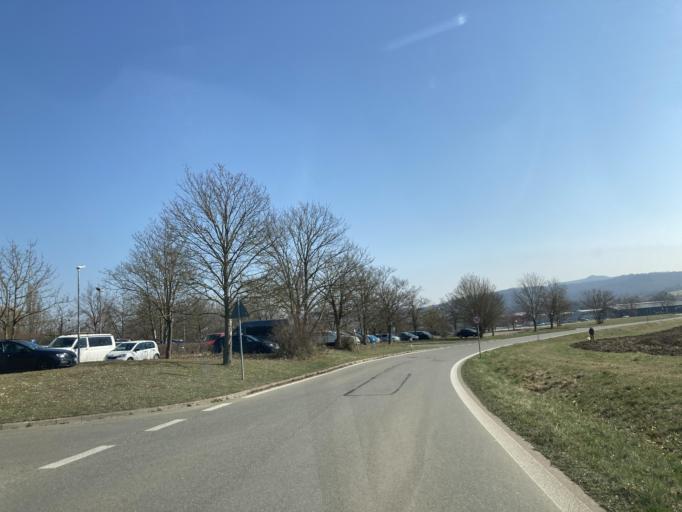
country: DE
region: Baden-Wuerttemberg
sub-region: Tuebingen Region
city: Nehren
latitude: 48.4452
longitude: 9.0751
